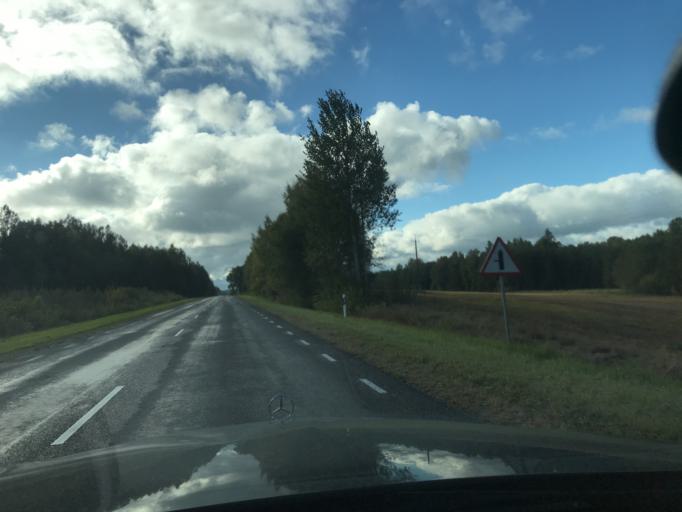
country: EE
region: Tartu
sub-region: Elva linn
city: Elva
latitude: 57.9855
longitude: 26.2620
